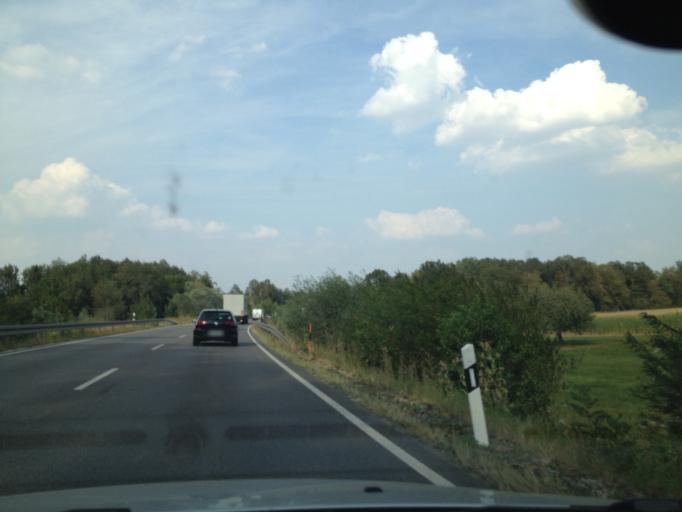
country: DE
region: Bavaria
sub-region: Swabia
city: Buchdorf
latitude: 48.7907
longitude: 10.8109
